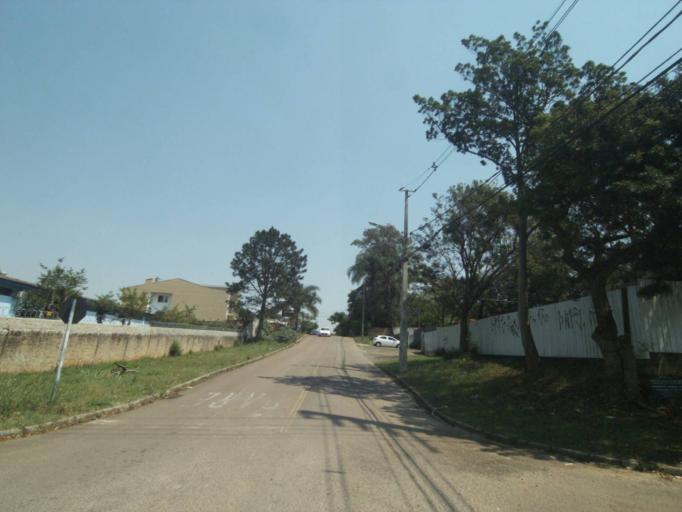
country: BR
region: Parana
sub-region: Sao Jose Dos Pinhais
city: Sao Jose dos Pinhais
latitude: -25.4996
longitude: -49.2705
